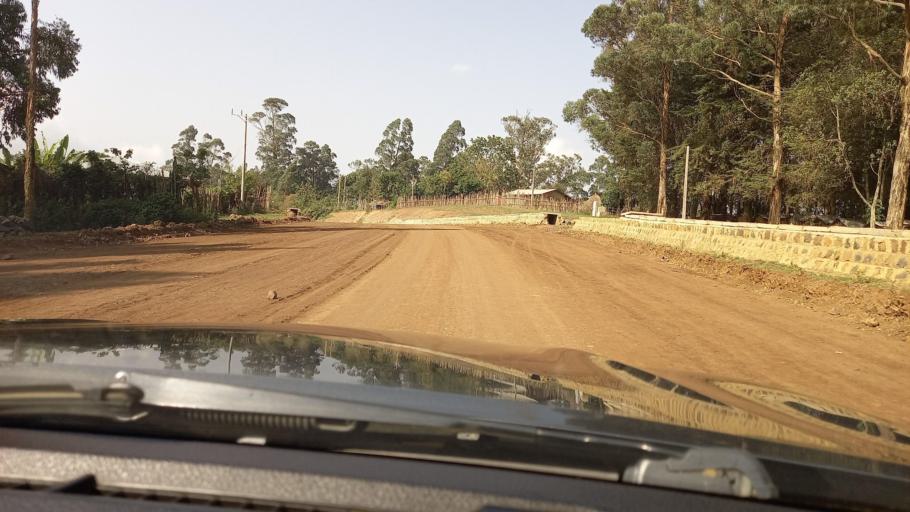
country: ET
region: Southern Nations, Nationalities, and People's Region
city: Mizan Teferi
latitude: 6.1706
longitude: 35.5854
